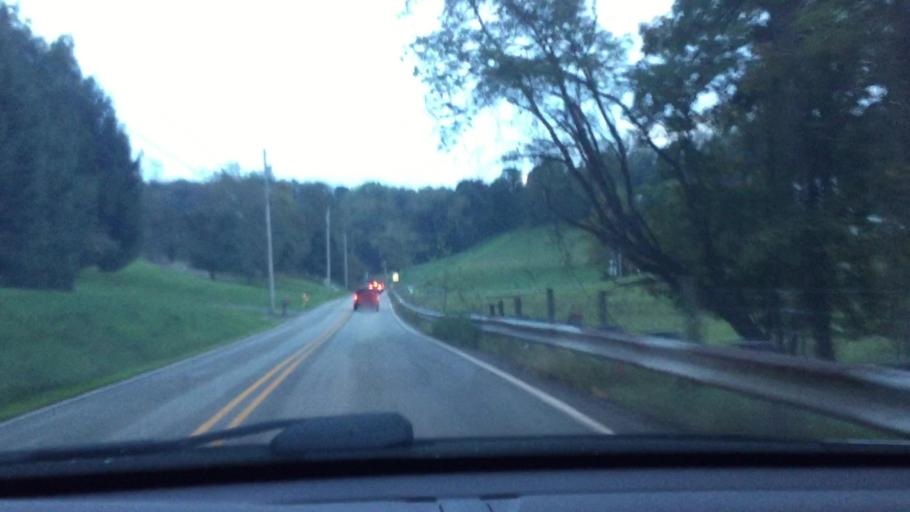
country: US
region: Pennsylvania
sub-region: Washington County
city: McGovern
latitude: 40.1912
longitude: -80.1935
